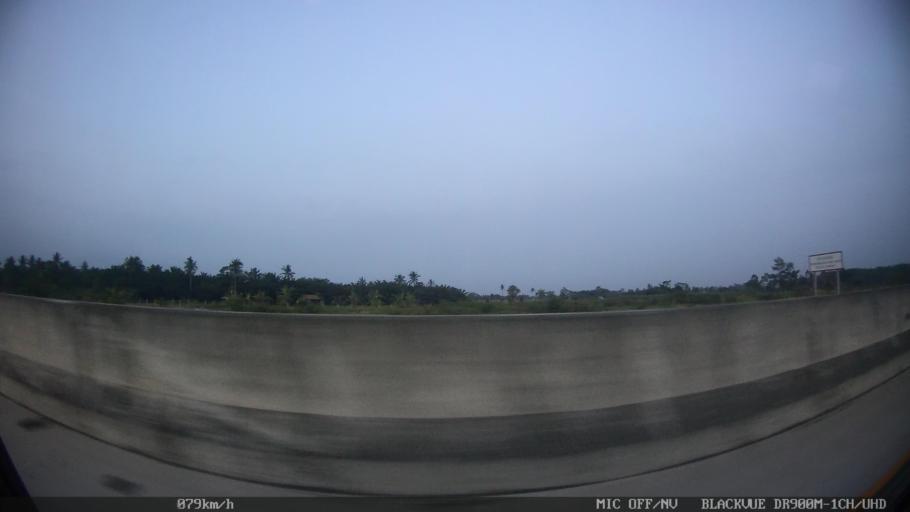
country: ID
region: Lampung
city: Sidorejo
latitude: -5.6247
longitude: 105.5643
